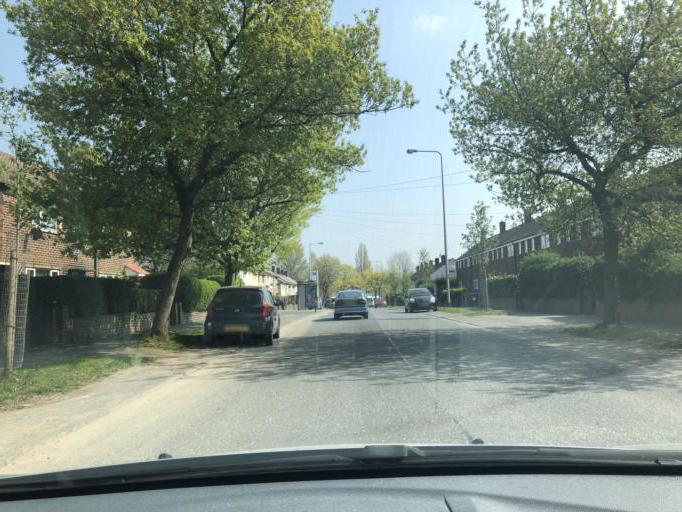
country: GB
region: England
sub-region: Borough of Stockport
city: Bredbury
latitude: 53.4308
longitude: -2.1322
